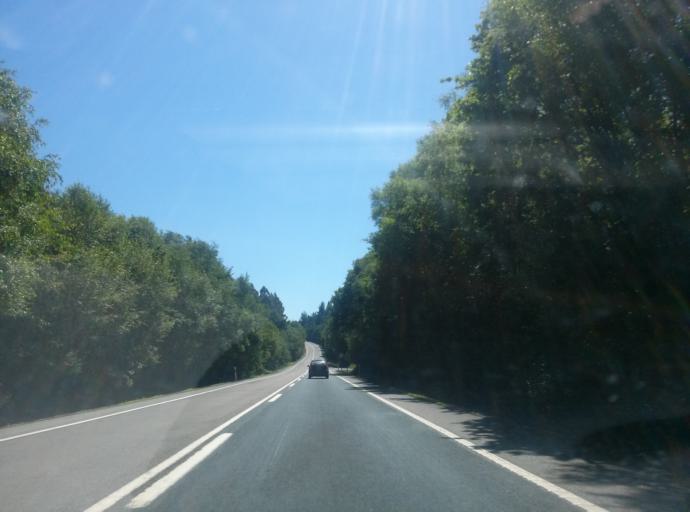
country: ES
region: Galicia
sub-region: Provincia de Lugo
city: Castro de Rei
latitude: 43.1474
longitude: -7.3966
